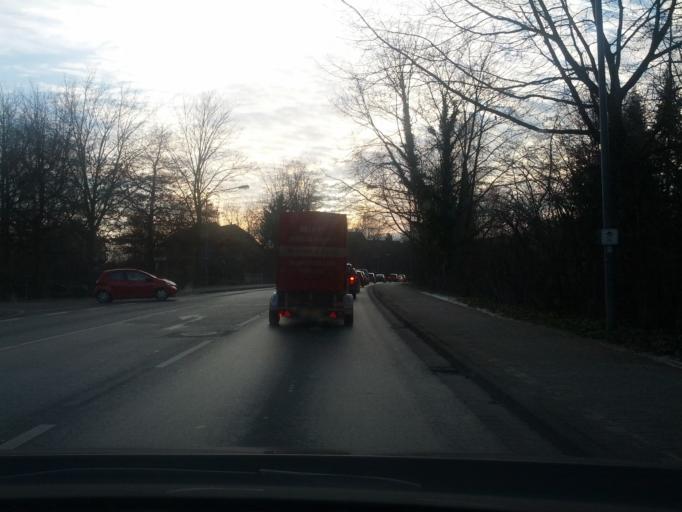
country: DE
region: Lower Saxony
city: Buxtehude
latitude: 53.4750
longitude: 9.7021
